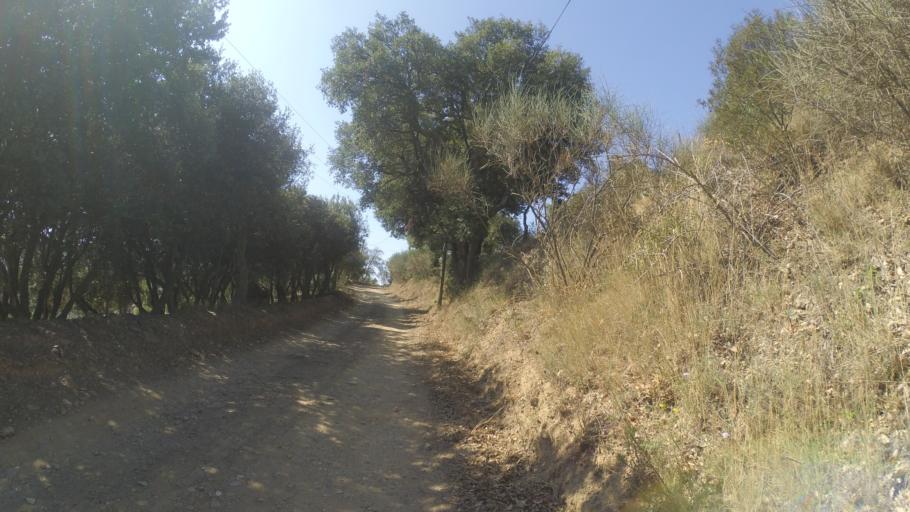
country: FR
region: Languedoc-Roussillon
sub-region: Departement des Pyrenees-Orientales
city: Millas
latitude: 42.6201
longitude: 2.6780
